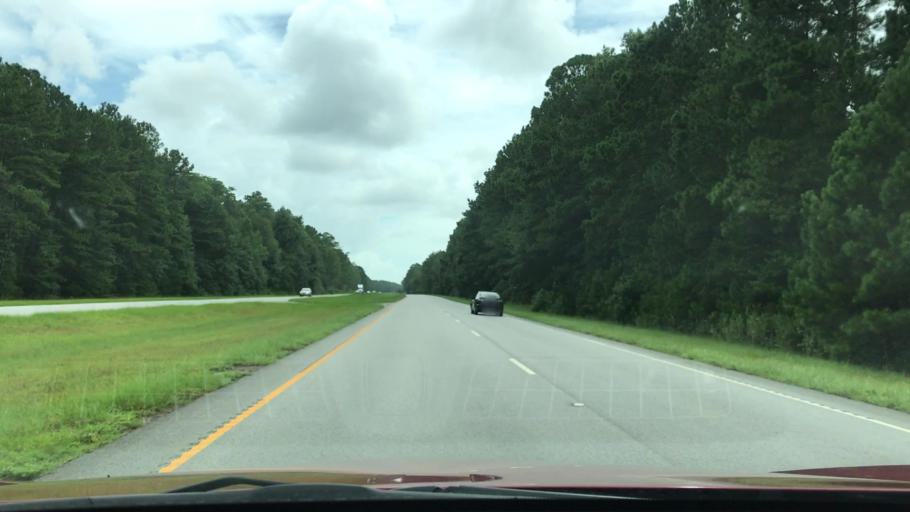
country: US
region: South Carolina
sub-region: Charleston County
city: Awendaw
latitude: 33.1361
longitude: -79.4431
